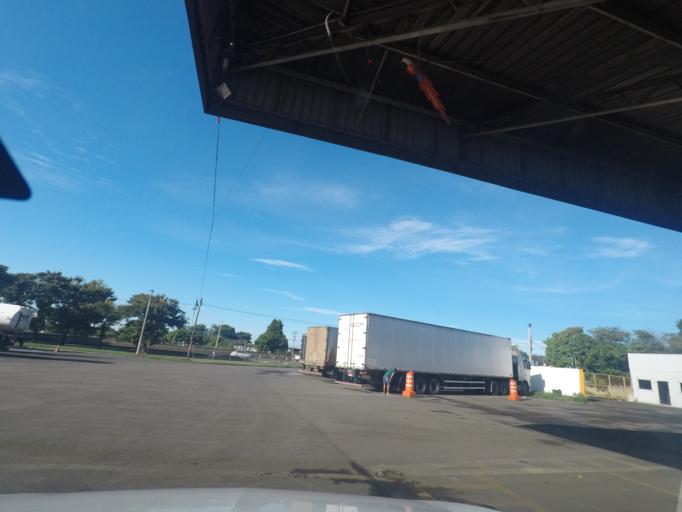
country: BR
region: Sao Paulo
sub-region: Nova Odessa
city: Nova Odessa
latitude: -22.7347
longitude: -47.2831
